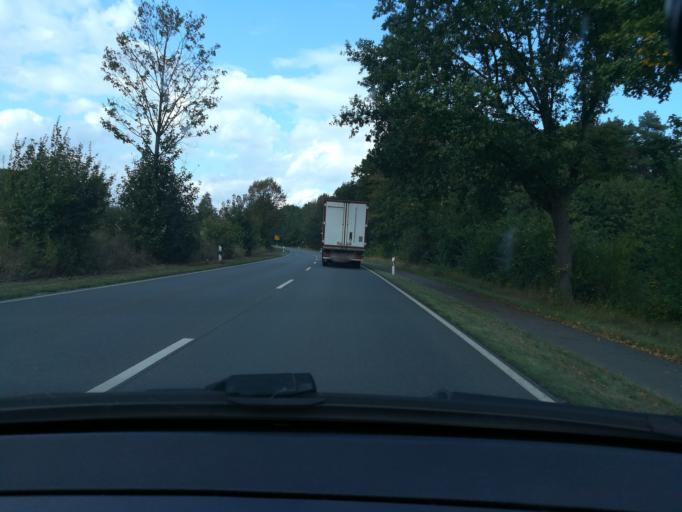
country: DE
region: North Rhine-Westphalia
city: Versmold
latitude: 52.0054
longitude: 8.1444
